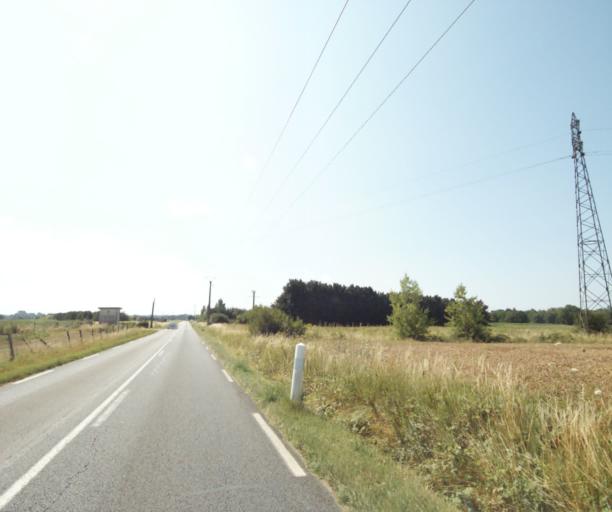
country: FR
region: Centre
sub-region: Departement du Loiret
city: Saint-Cyr-en-Val
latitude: 47.8447
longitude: 1.9582
